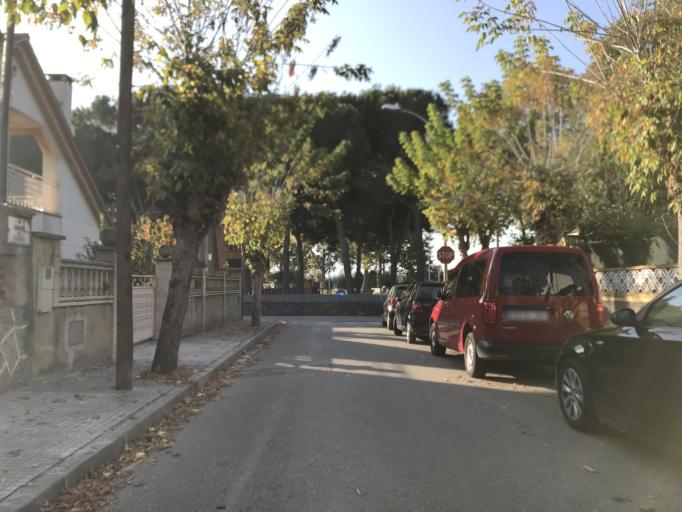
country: ES
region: Catalonia
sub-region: Provincia de Barcelona
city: Mollet del Valles
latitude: 41.5565
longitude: 2.2199
